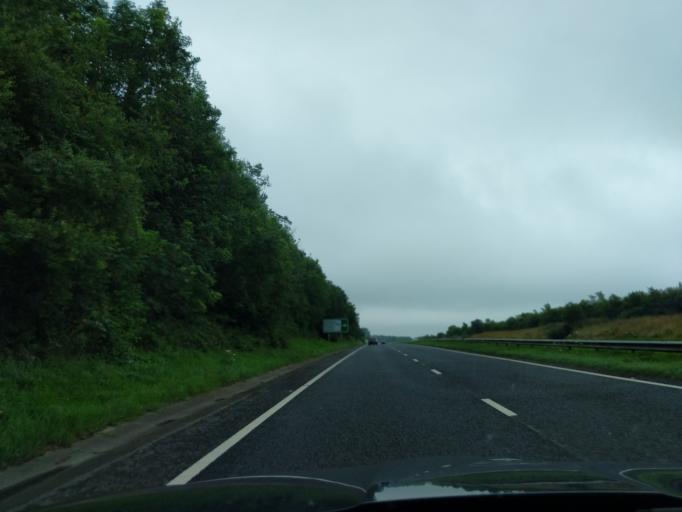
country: GB
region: England
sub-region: Northumberland
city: Ellingham
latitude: 55.5084
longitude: -1.7390
